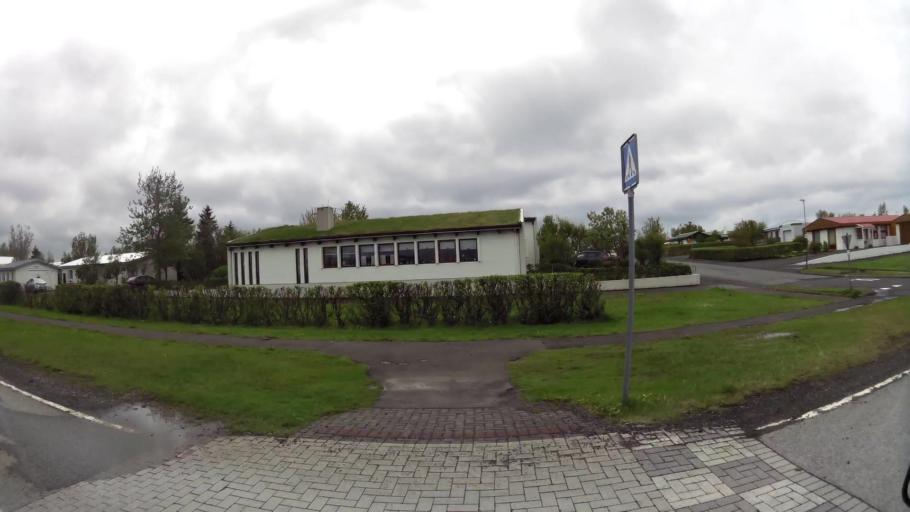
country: IS
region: Capital Region
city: Alftanes
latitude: 64.1097
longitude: -22.0140
